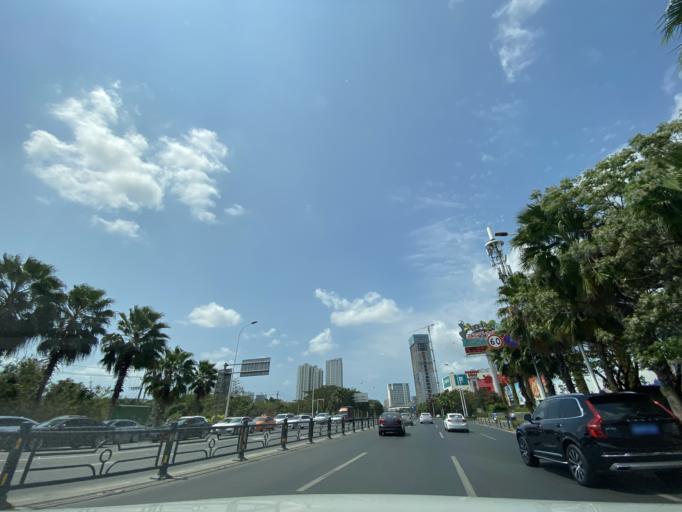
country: CN
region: Hainan
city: Tiandu
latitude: 18.2926
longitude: 109.5290
